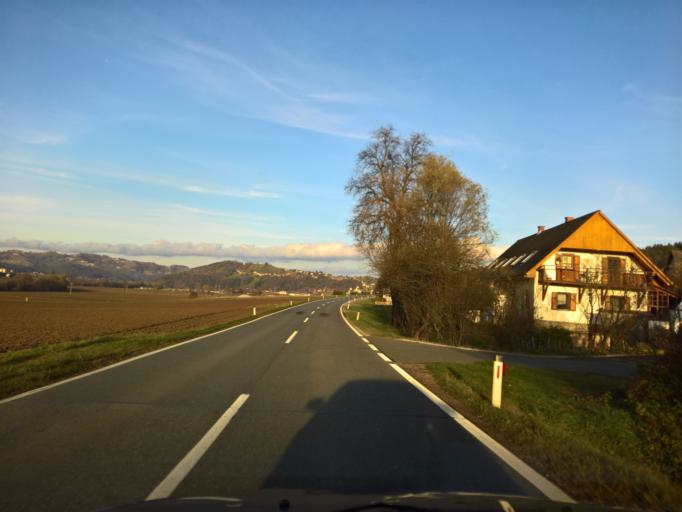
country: AT
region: Styria
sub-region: Politischer Bezirk Leibnitz
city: Grossklein
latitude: 46.7257
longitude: 15.4234
